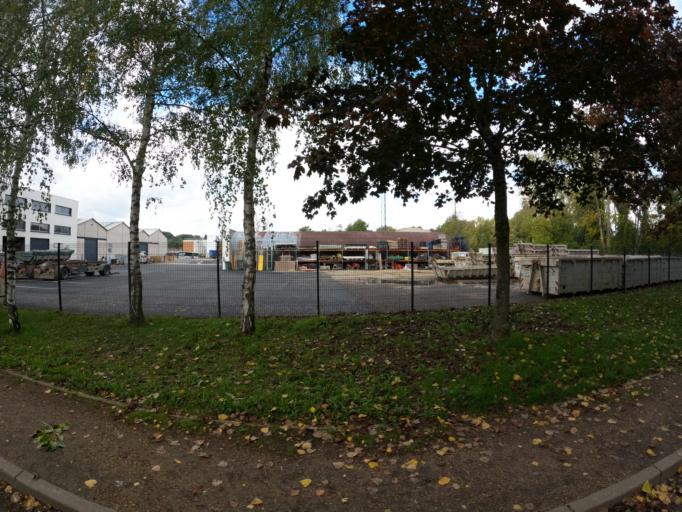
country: FR
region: Ile-de-France
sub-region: Departement de Seine-et-Marne
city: Montry
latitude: 48.8895
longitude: 2.8340
